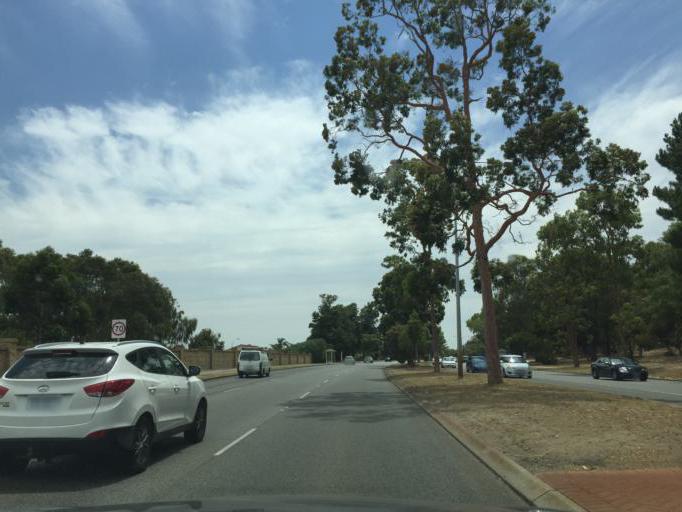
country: AU
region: Western Australia
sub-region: Melville
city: Winthrop
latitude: -32.0655
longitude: 115.8298
